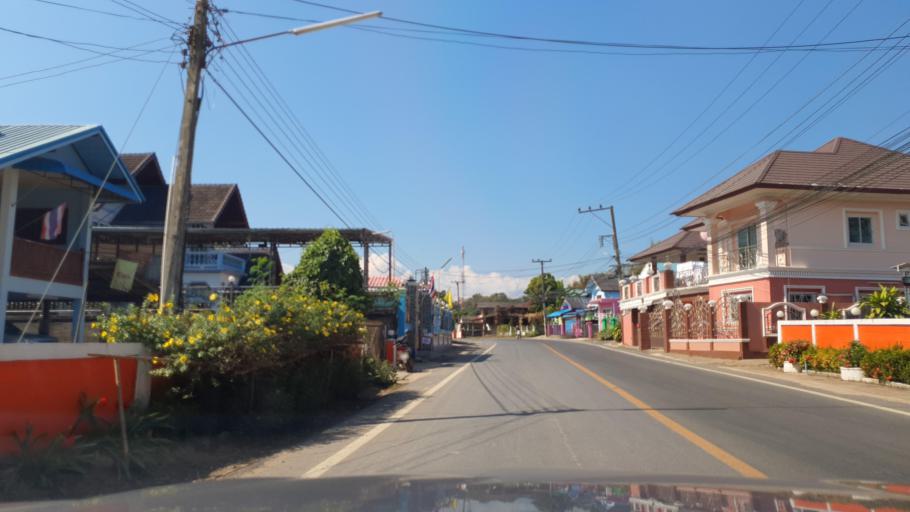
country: TH
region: Nan
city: Tha Wang Pha
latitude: 19.0816
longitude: 100.8832
